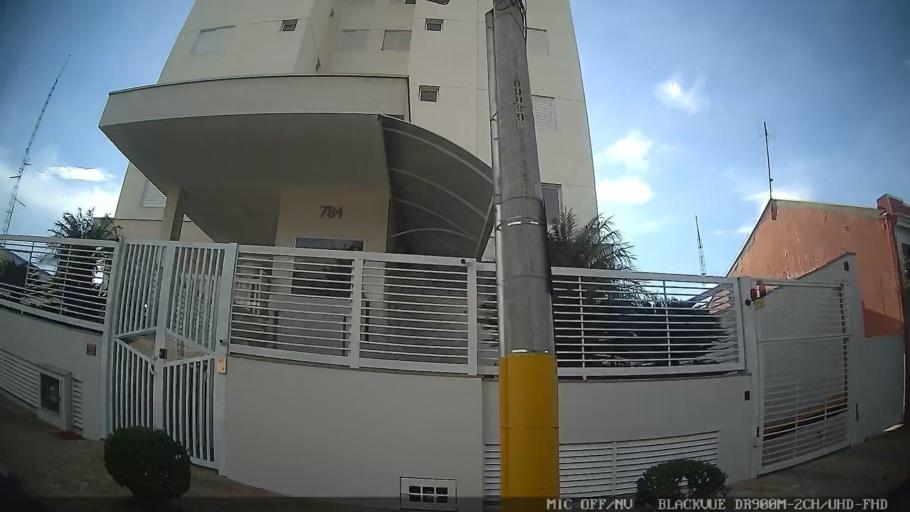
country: BR
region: Sao Paulo
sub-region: Tiete
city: Tiete
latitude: -23.1062
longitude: -47.7153
